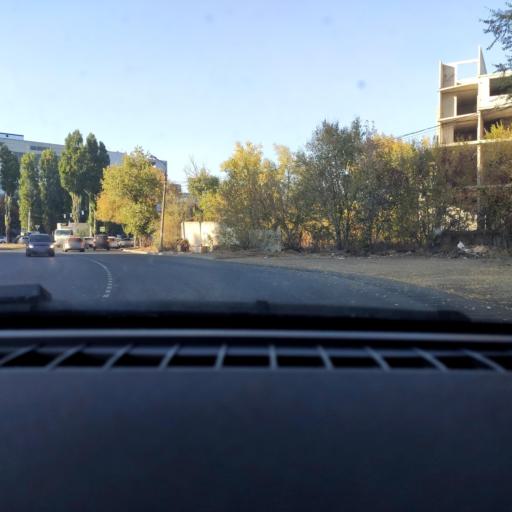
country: RU
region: Voronezj
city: Voronezh
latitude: 51.6748
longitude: 39.2574
